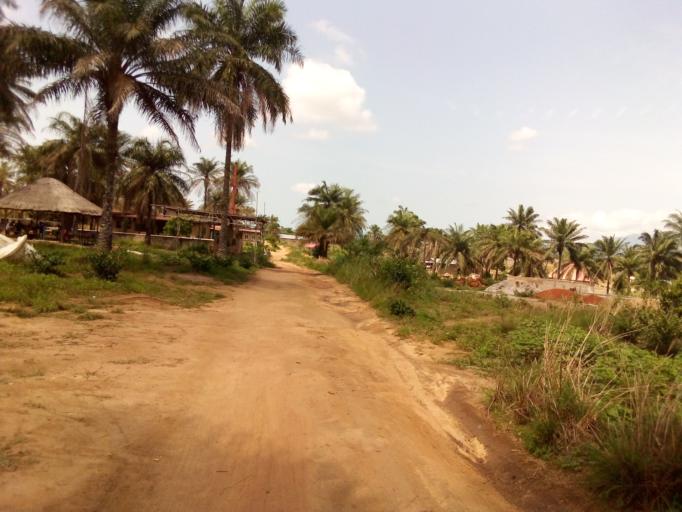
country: SL
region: Western Area
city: Waterloo
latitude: 8.3477
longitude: -13.0162
